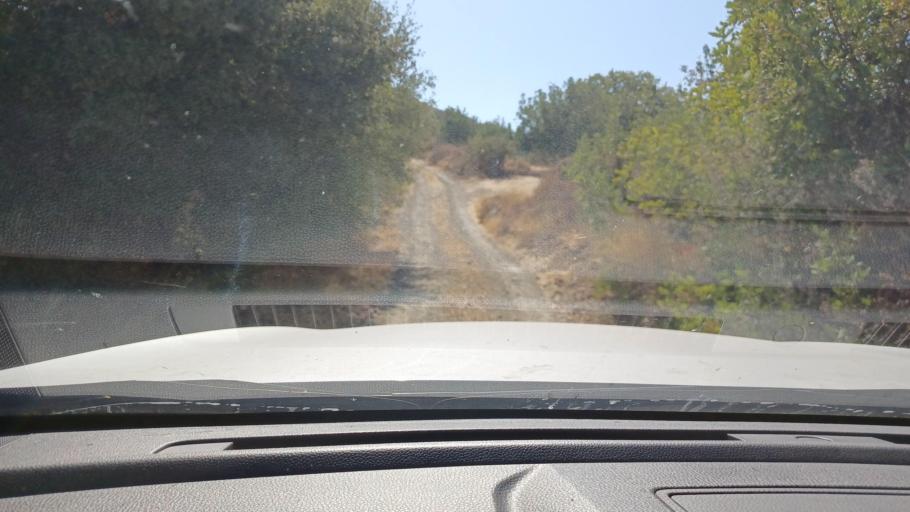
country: CY
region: Pafos
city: Polis
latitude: 34.9993
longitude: 32.5000
